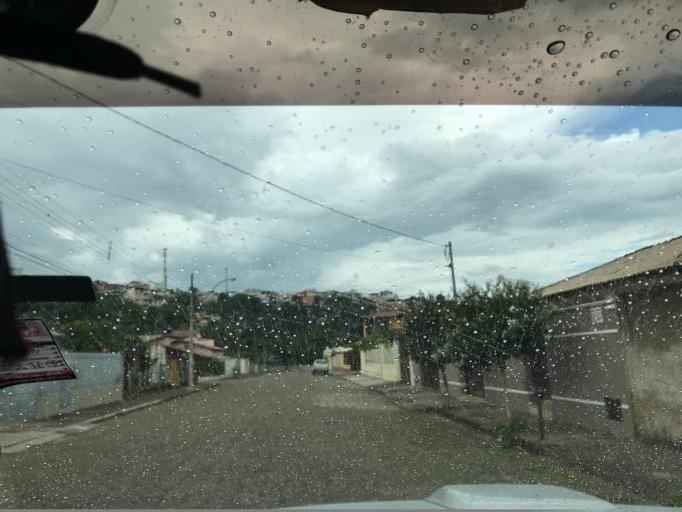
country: BR
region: Minas Gerais
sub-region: Tres Coracoes
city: Tres Coracoes
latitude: -21.7005
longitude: -45.2504
